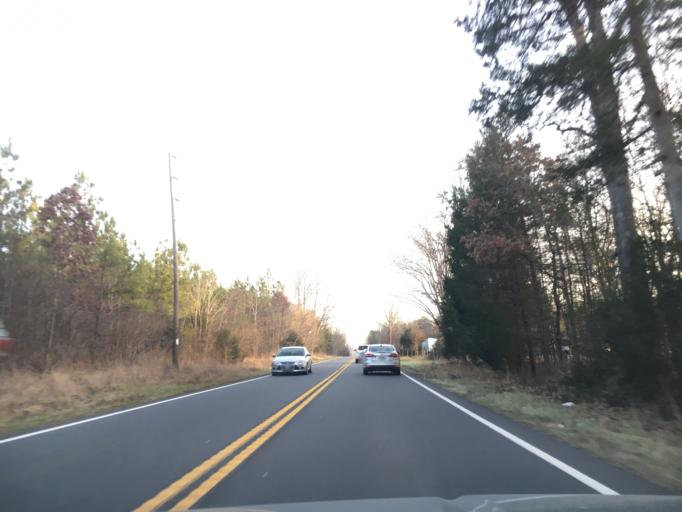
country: US
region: Virginia
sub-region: Culpeper County
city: Culpeper
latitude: 38.3688
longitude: -77.9786
